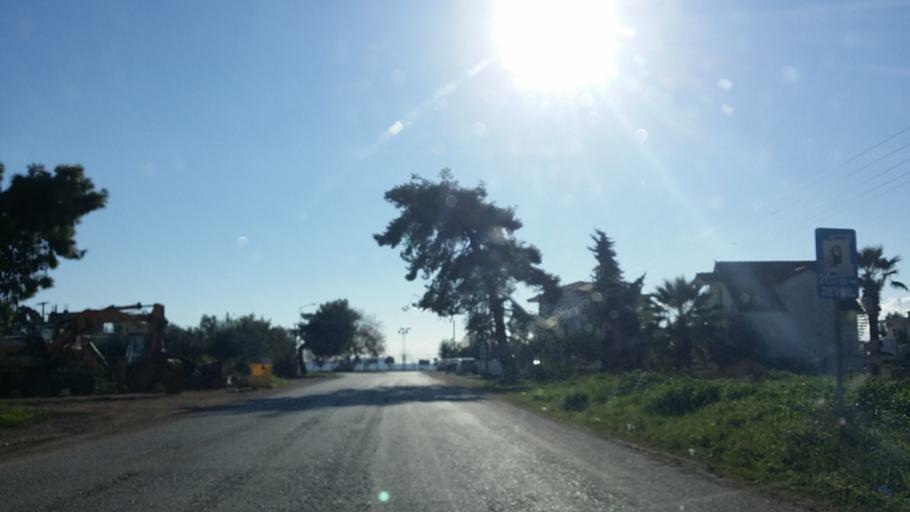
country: GR
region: West Greece
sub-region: Nomos Aitolias kai Akarnanias
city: Astakos
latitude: 38.5365
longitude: 21.0897
